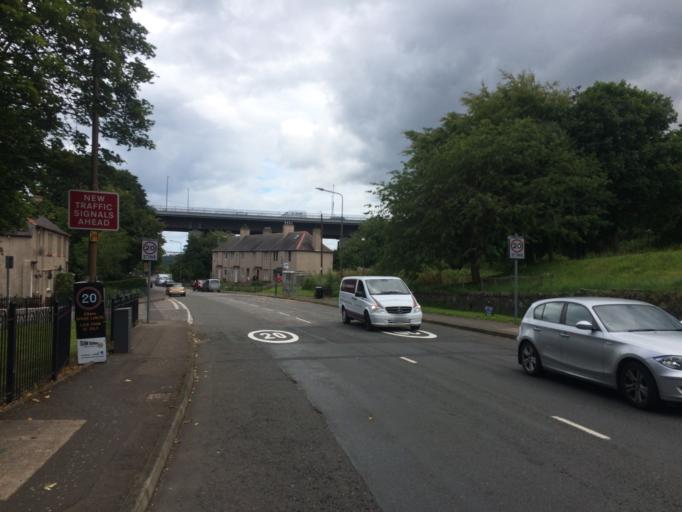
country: GB
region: Scotland
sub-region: Edinburgh
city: Queensferry
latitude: 55.9897
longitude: -3.4070
